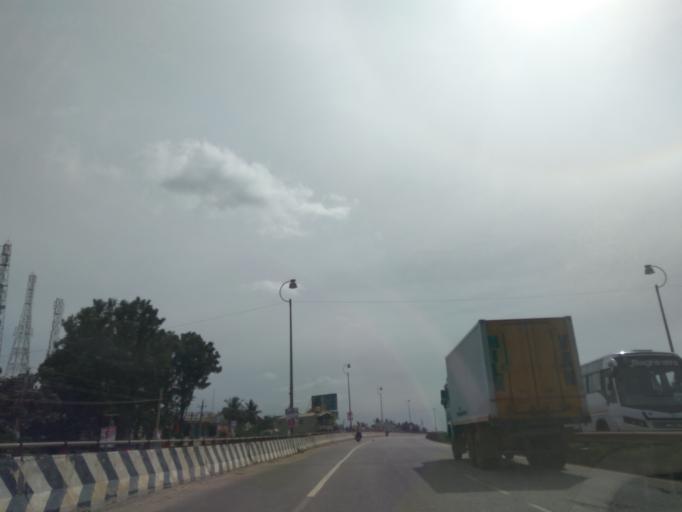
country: IN
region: Karnataka
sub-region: Bangalore Rural
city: Dasarahalli
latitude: 13.1322
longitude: 77.9277
